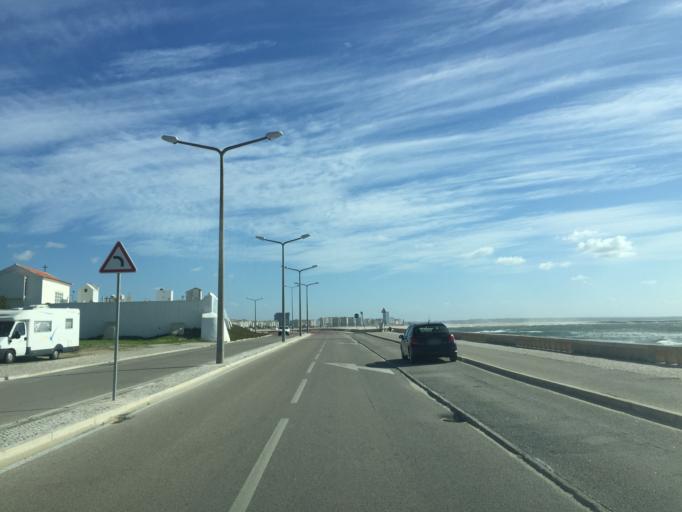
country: PT
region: Coimbra
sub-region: Figueira da Foz
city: Buarcos
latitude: 40.1674
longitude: -8.8857
